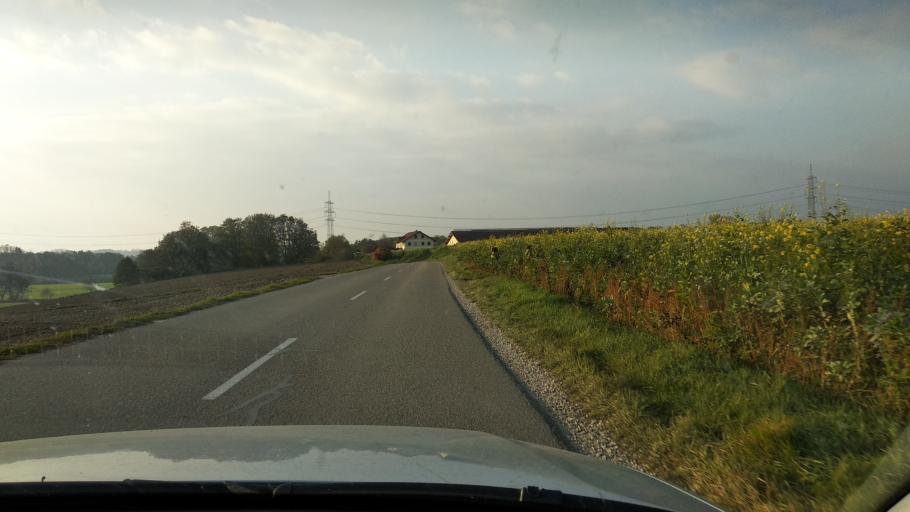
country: DE
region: Bavaria
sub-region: Upper Bavaria
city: Pastetten
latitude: 48.2153
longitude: 11.9286
